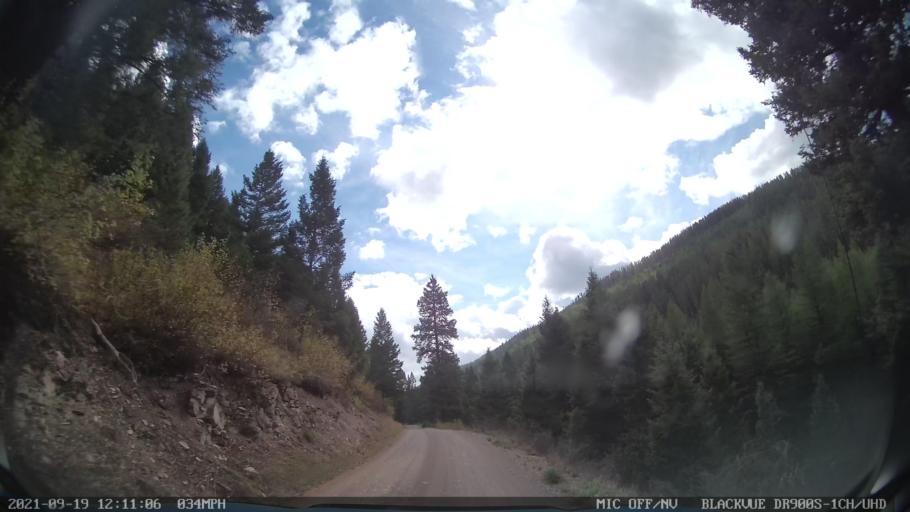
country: US
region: Montana
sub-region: Missoula County
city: Seeley Lake
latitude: 47.1761
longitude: -113.3765
